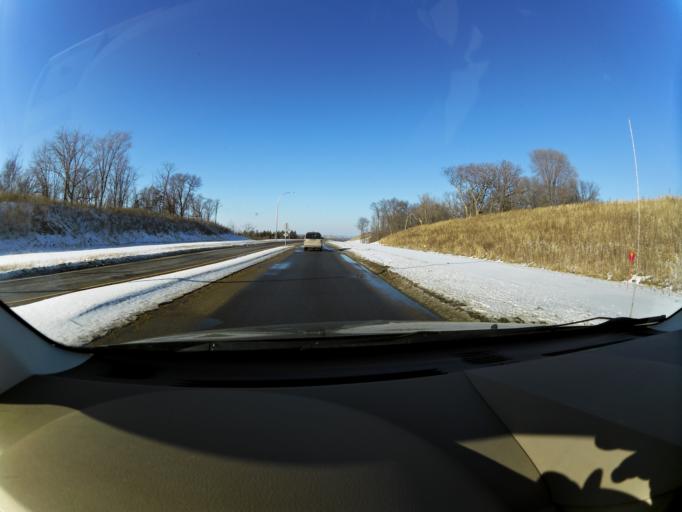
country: US
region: Minnesota
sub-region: Goodhue County
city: Cannon Falls
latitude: 44.4825
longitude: -92.9029
